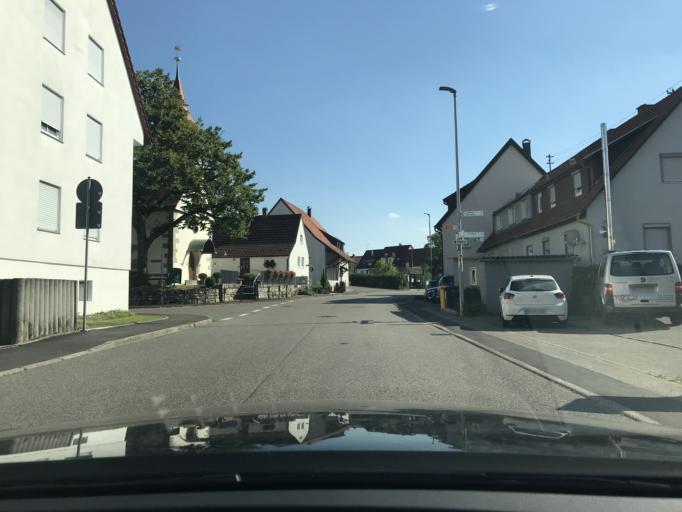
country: DE
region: Baden-Wuerttemberg
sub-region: Regierungsbezirk Stuttgart
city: Winterbach
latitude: 48.7723
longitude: 9.5033
